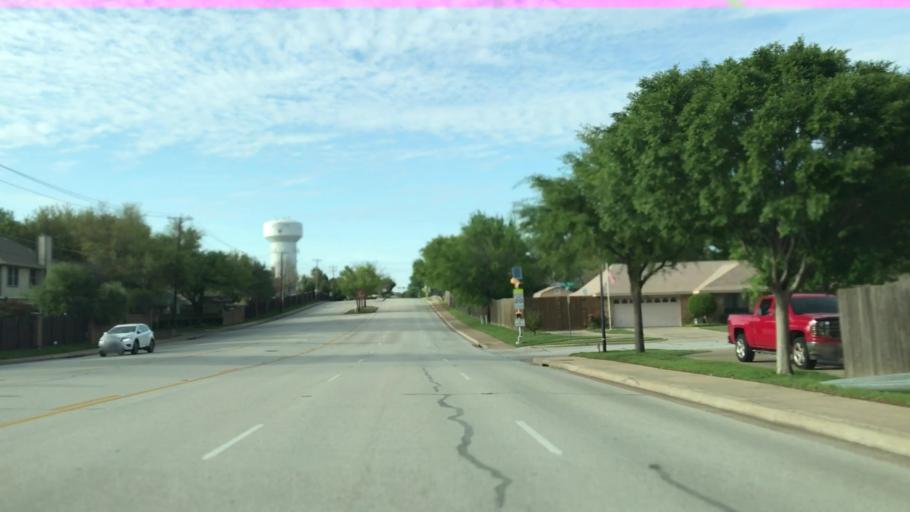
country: US
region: Texas
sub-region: Tarrant County
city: Grapevine
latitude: 32.9518
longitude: -97.0982
